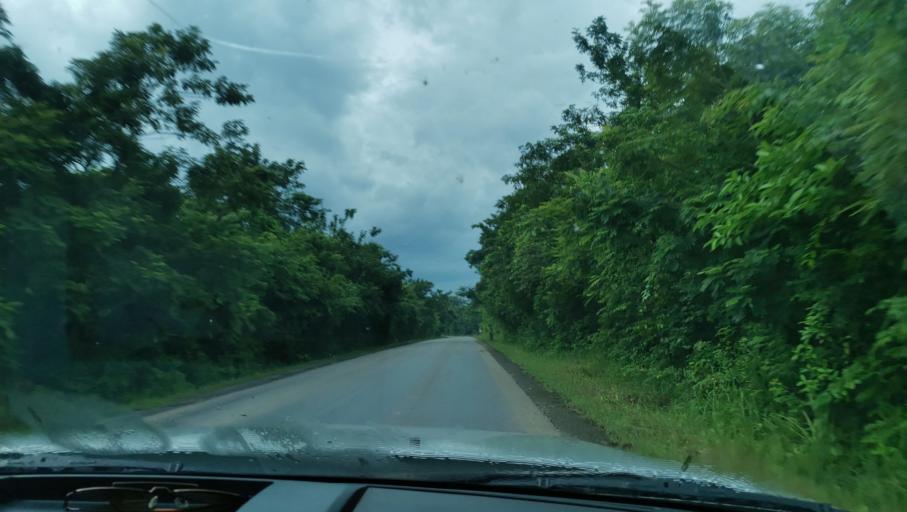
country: TH
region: Nakhon Phanom
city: Ban Phaeng
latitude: 17.8757
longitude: 104.4133
